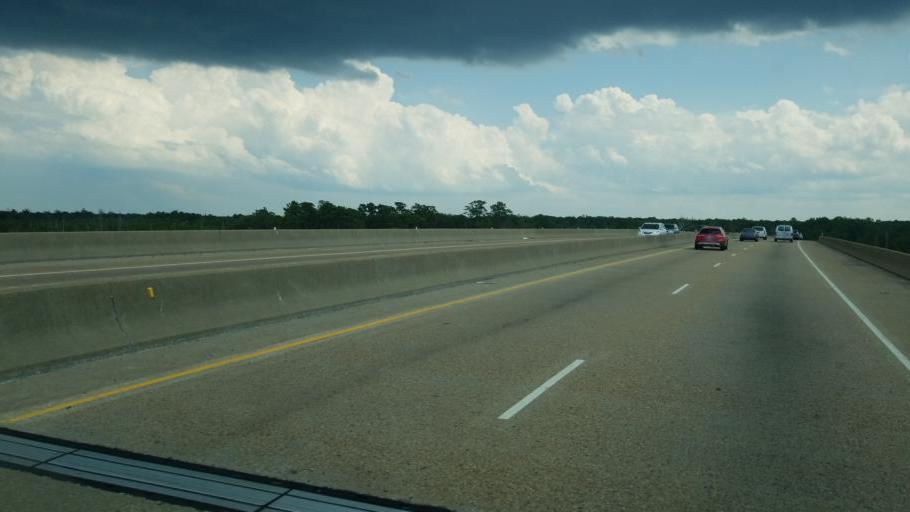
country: US
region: Virginia
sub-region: City of Chesapeake
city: Chesapeake
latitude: 36.7216
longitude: -76.2265
